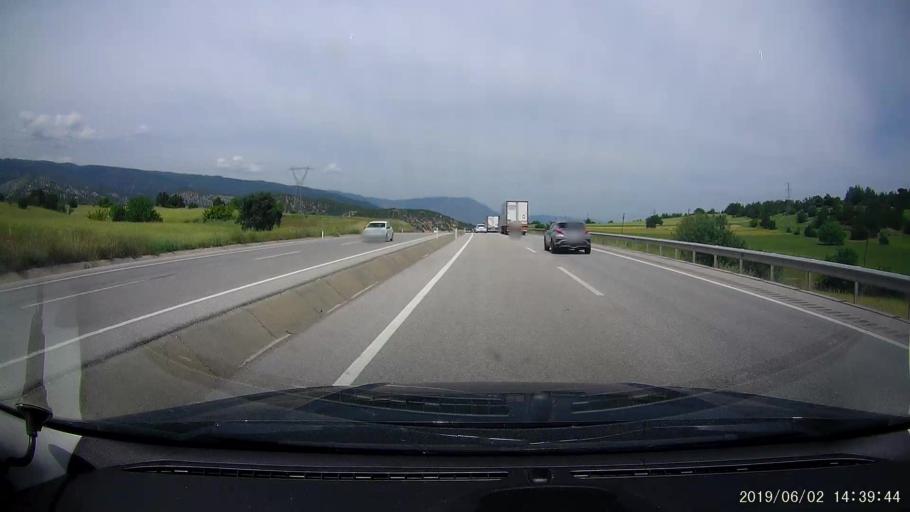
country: TR
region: Corum
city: Hacihamza
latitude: 41.0736
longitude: 34.3064
